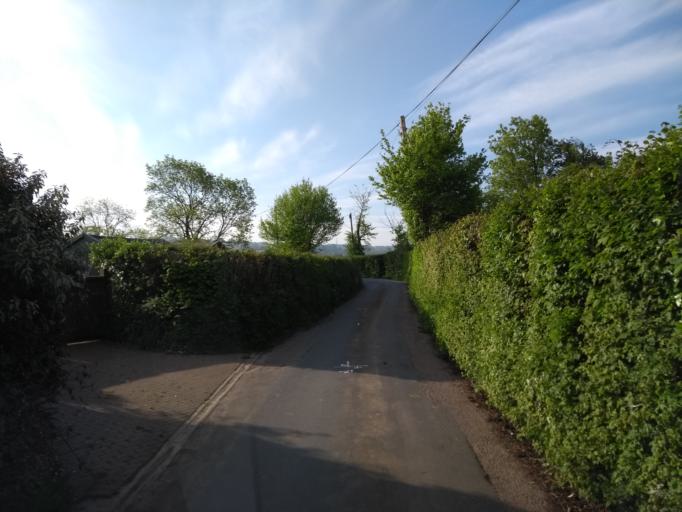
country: GB
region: England
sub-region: Devon
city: Axminster
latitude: 50.8053
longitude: -2.9504
